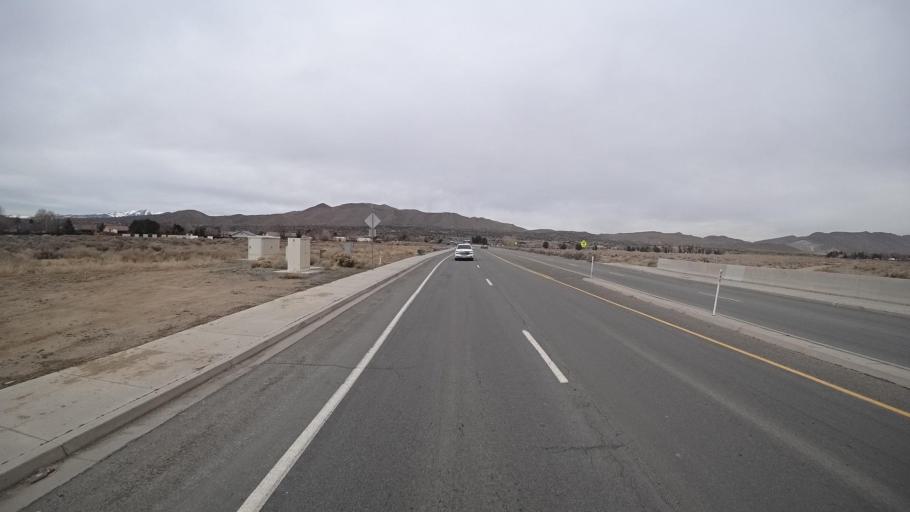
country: US
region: Nevada
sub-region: Washoe County
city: Spanish Springs
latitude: 39.6399
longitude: -119.7151
